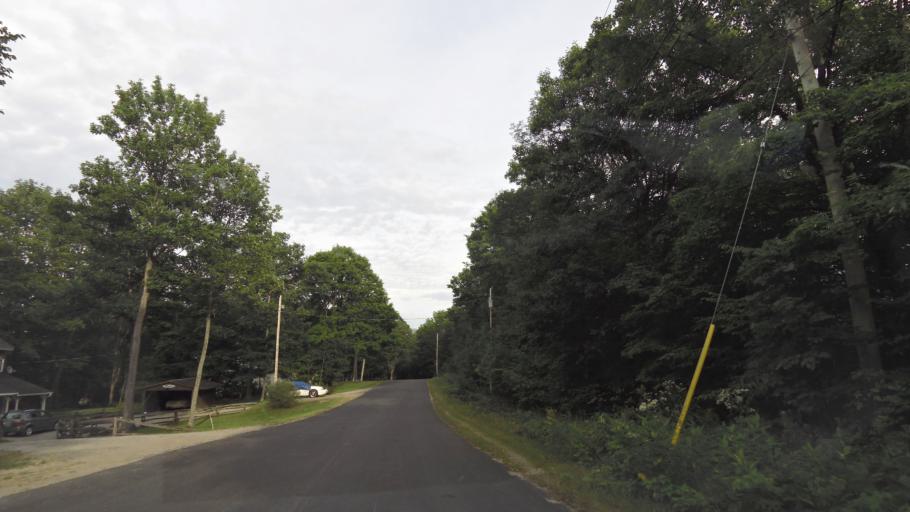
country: CA
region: Ontario
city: Bancroft
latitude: 45.0429
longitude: -78.4990
